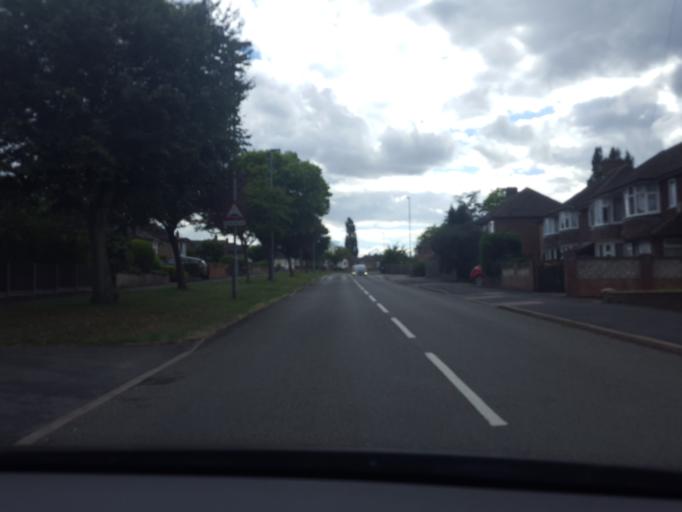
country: GB
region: England
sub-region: Leicestershire
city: Loughborough
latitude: 52.7536
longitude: -1.2141
